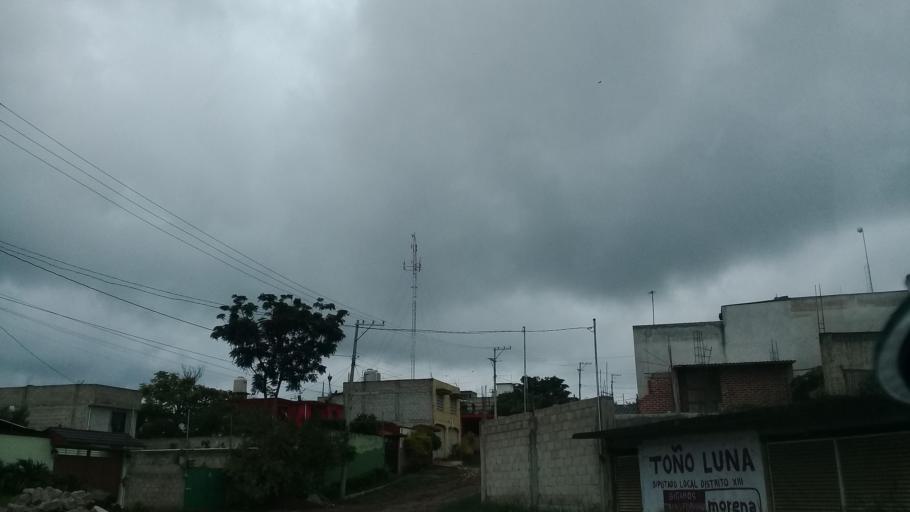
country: MX
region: Veracruz
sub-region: Emiliano Zapata
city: Las Trancas
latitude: 19.4967
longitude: -96.8615
